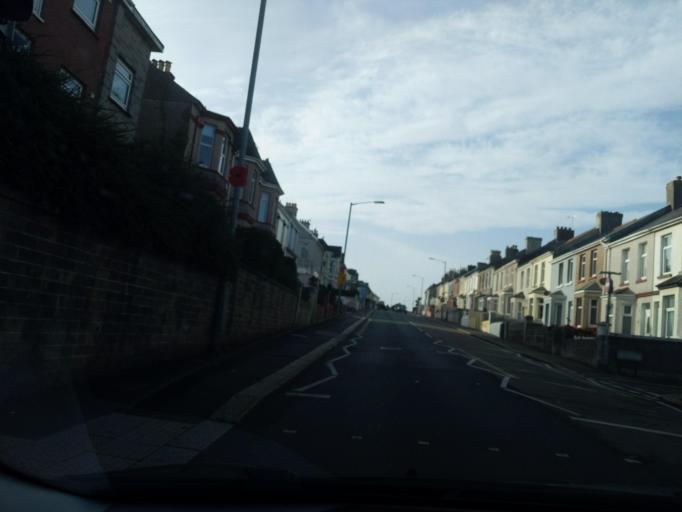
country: GB
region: England
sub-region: Cornwall
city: Torpoint
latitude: 50.3767
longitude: -4.1999
